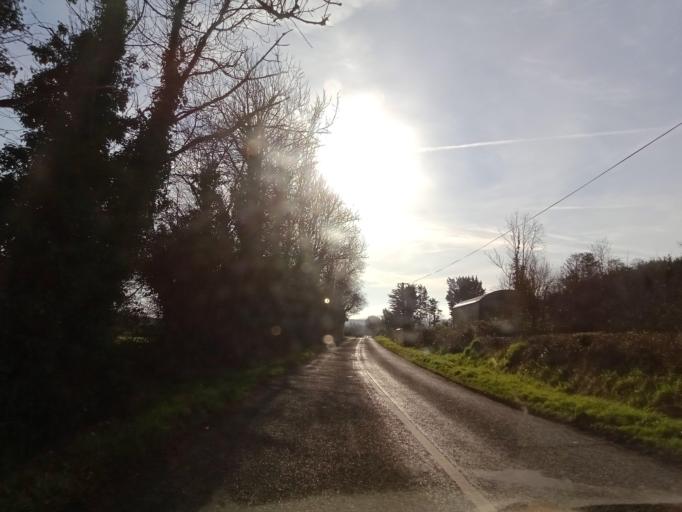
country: IE
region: Munster
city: Fethard
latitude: 52.5739
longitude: -7.5650
